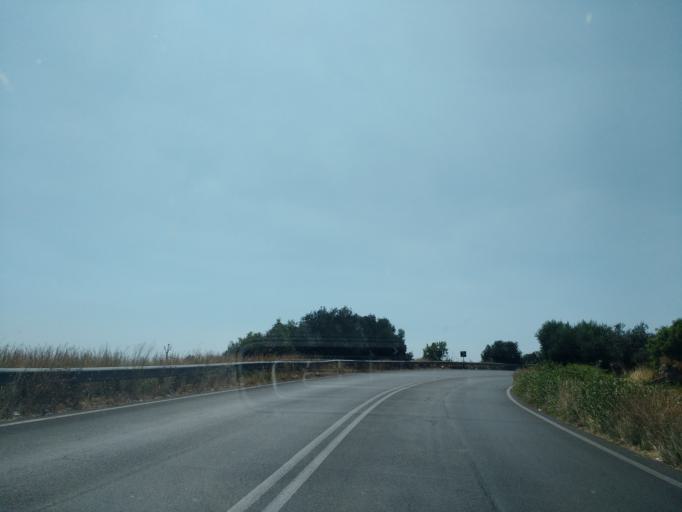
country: IT
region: Latium
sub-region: Citta metropolitana di Roma Capitale
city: Tivoli
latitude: 41.9490
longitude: 12.7924
